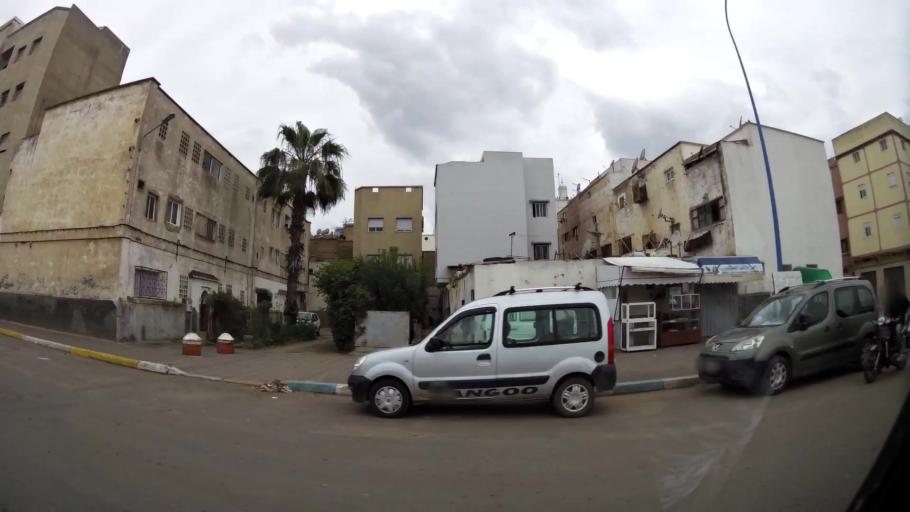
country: MA
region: Grand Casablanca
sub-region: Casablanca
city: Casablanca
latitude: 33.5685
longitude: -7.5661
